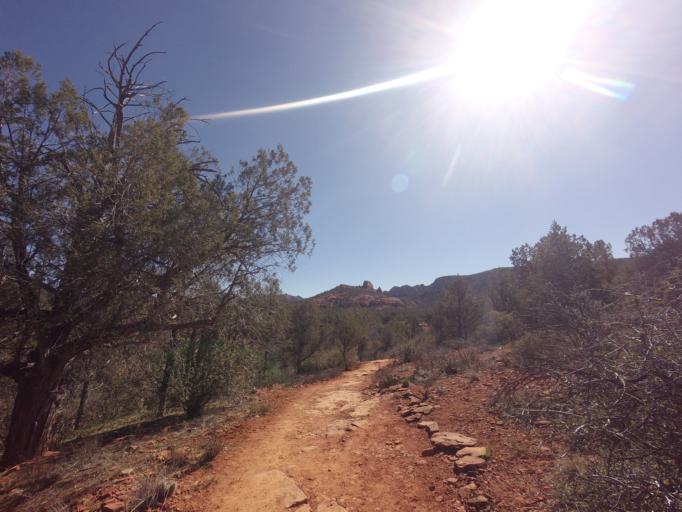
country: US
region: Arizona
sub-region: Yavapai County
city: West Sedona
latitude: 34.8069
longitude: -111.8251
